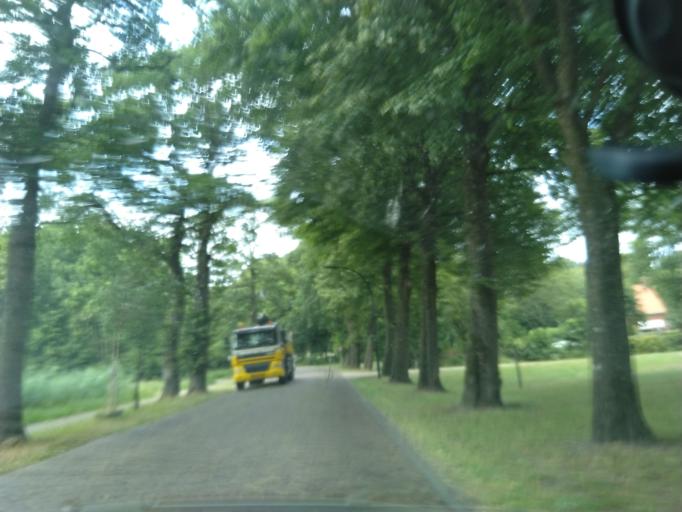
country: NL
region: Groningen
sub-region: Gemeente Vlagtwedde
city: Vlagtwedde
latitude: 53.0929
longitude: 7.1424
